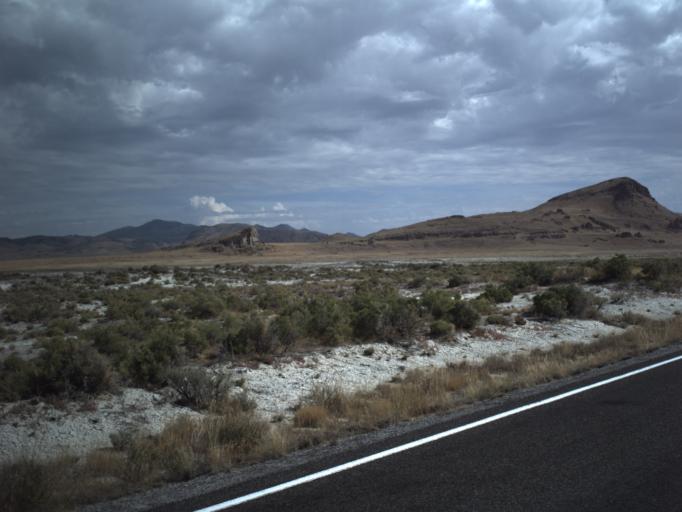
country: US
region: Utah
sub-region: Tooele County
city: Wendover
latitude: 41.4243
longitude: -113.8630
